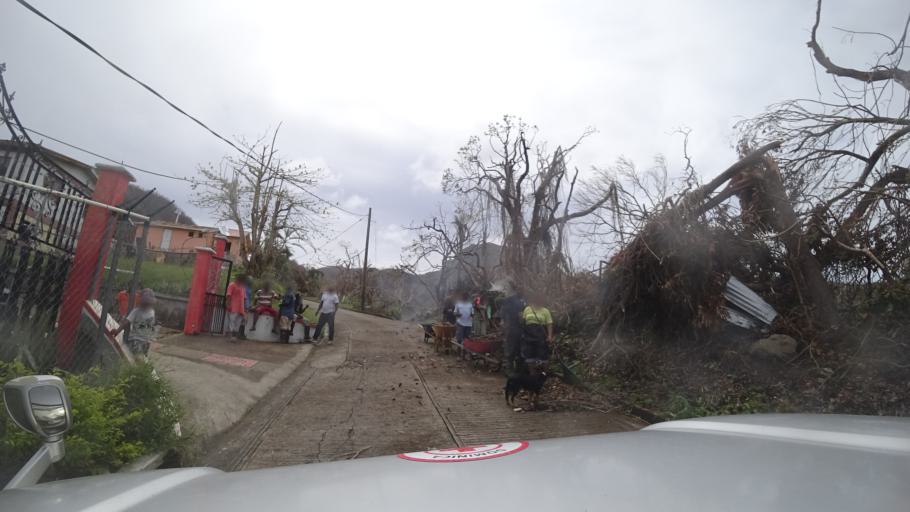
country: DM
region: Saint John
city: Portsmouth
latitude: 15.6142
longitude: -61.4099
